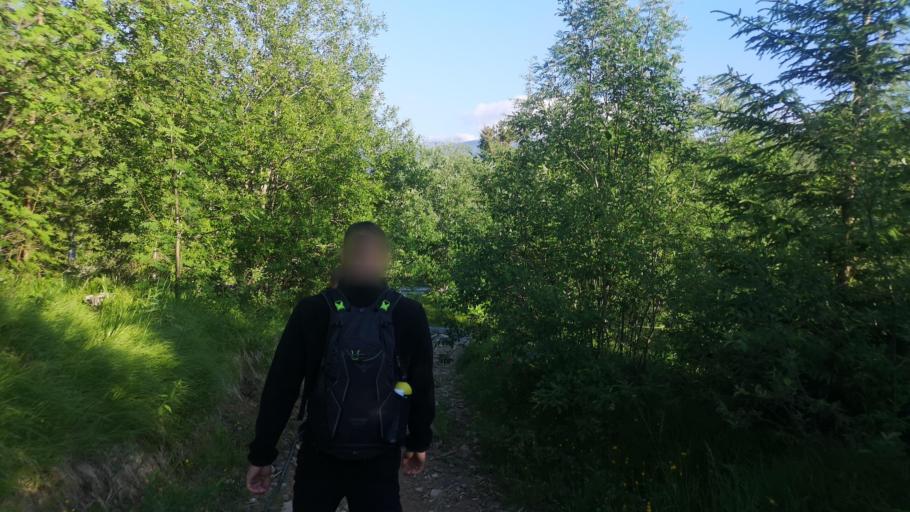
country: SK
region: Presovsky
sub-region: Okres Poprad
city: Strba
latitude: 49.1376
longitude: 19.9680
